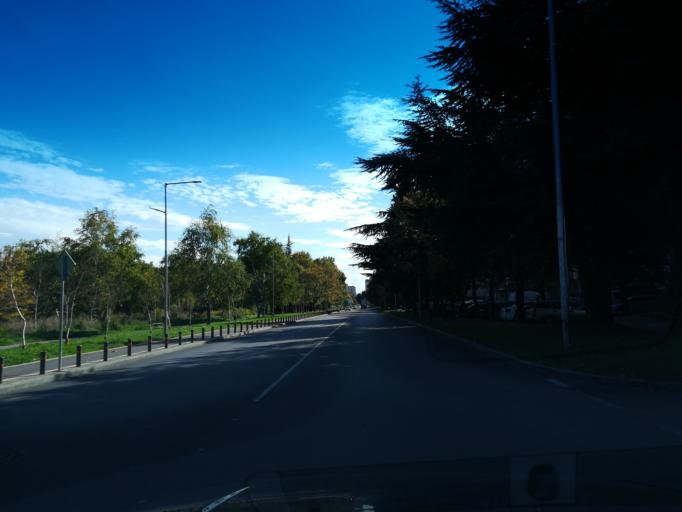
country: BG
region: Stara Zagora
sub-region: Obshtina Stara Zagora
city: Stara Zagora
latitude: 42.4373
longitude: 25.6360
